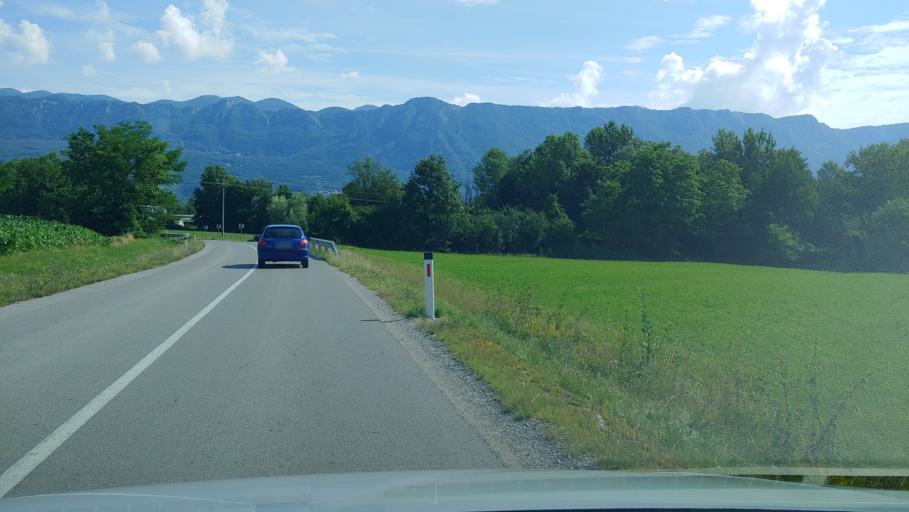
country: SI
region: Ajdovscina
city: Lokavec
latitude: 45.8827
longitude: 13.8749
